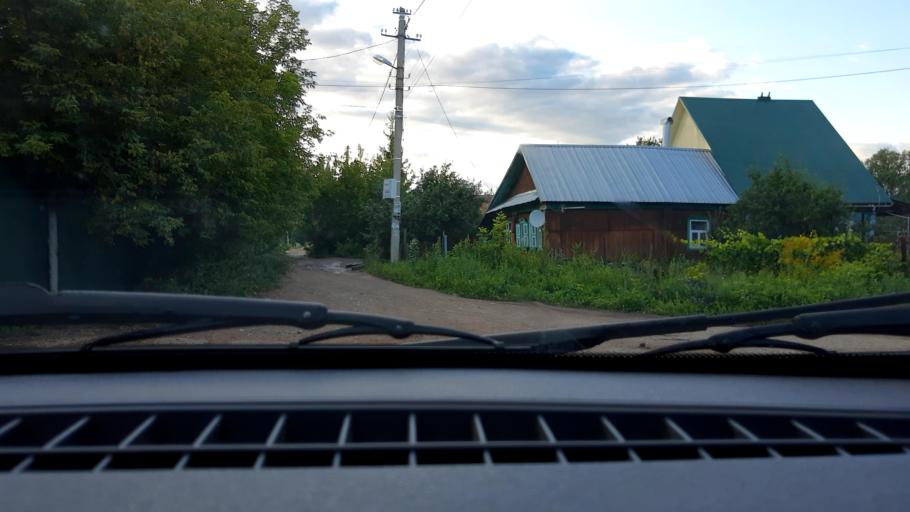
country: RU
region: Bashkortostan
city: Mikhaylovka
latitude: 54.7839
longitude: 55.8809
